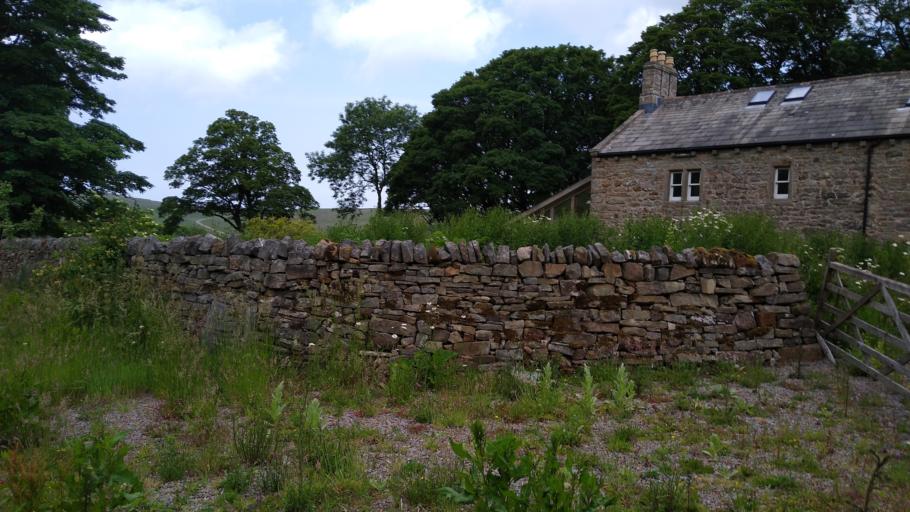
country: GB
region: England
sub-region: Northumberland
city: Greenhead
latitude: 54.9193
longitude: -2.6165
